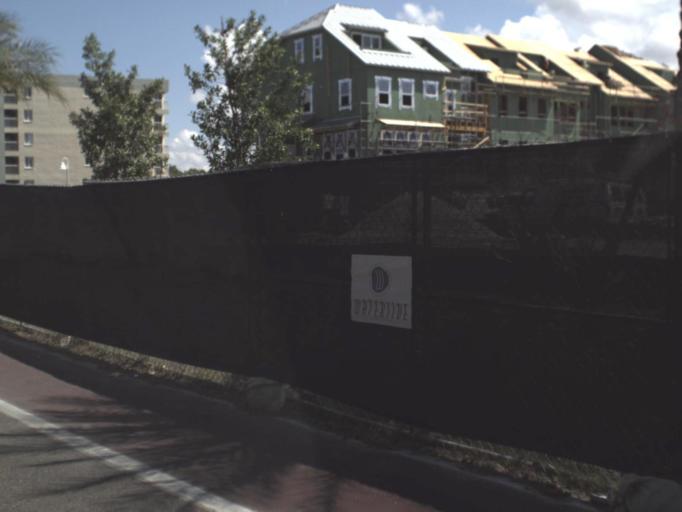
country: US
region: Florida
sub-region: Pinellas County
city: Indian Shores
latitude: 27.8634
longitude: -82.8482
